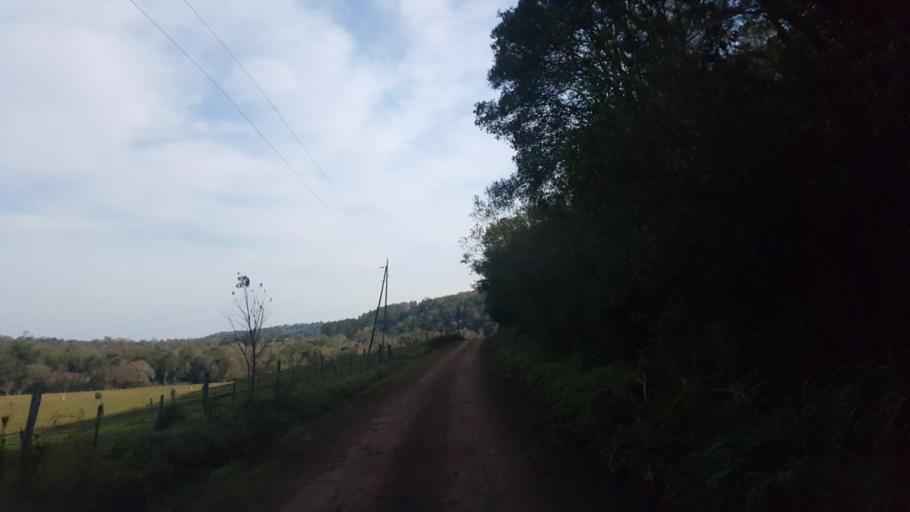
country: AR
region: Misiones
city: Capiovi
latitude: -26.9133
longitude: -55.0829
